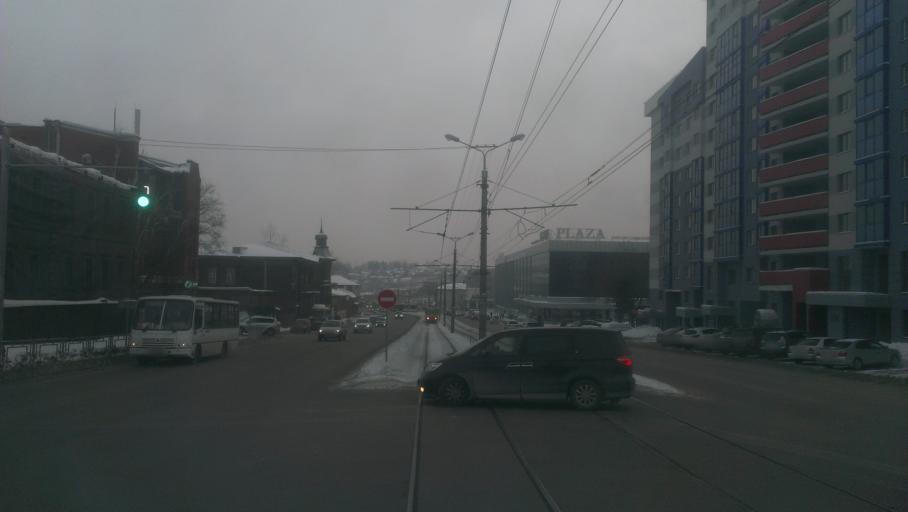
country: RU
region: Altai Krai
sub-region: Gorod Barnaulskiy
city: Barnaul
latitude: 53.3323
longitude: 83.7806
